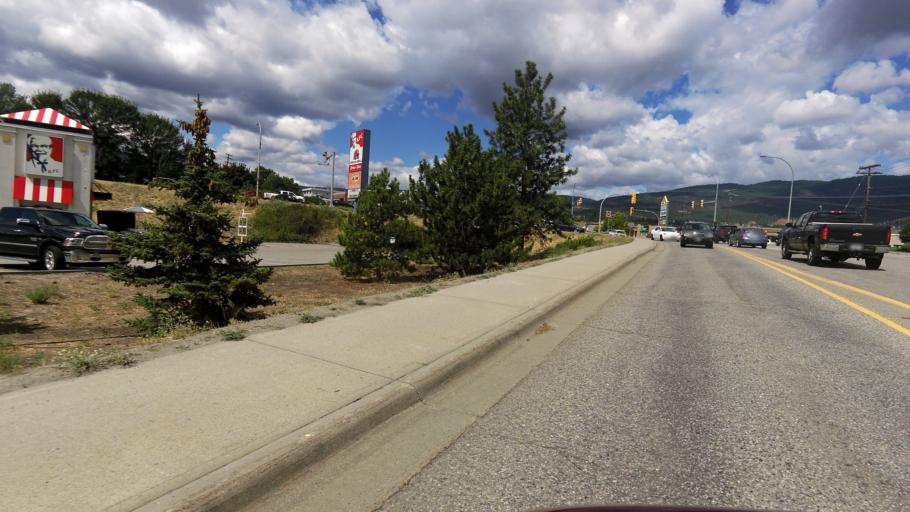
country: CA
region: British Columbia
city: West Kelowna
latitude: 49.8304
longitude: -119.6221
